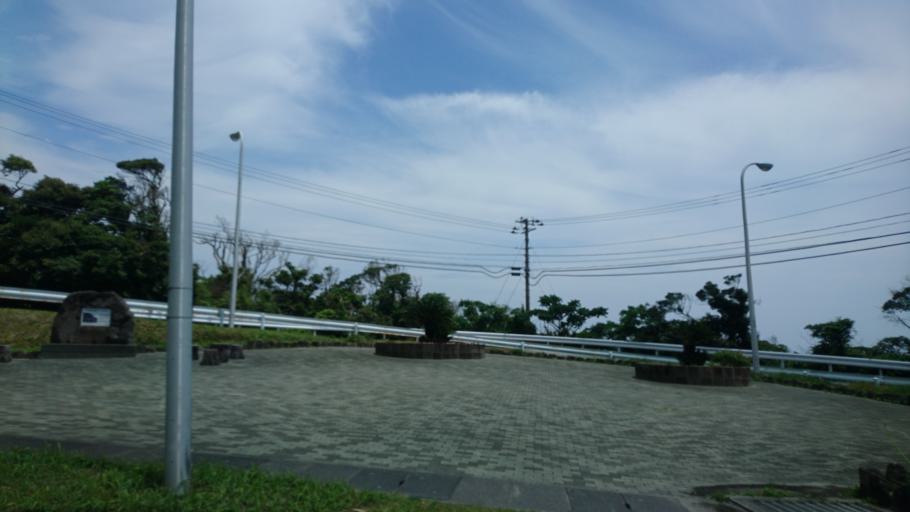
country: JP
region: Shizuoka
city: Shimoda
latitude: 34.3853
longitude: 139.2738
